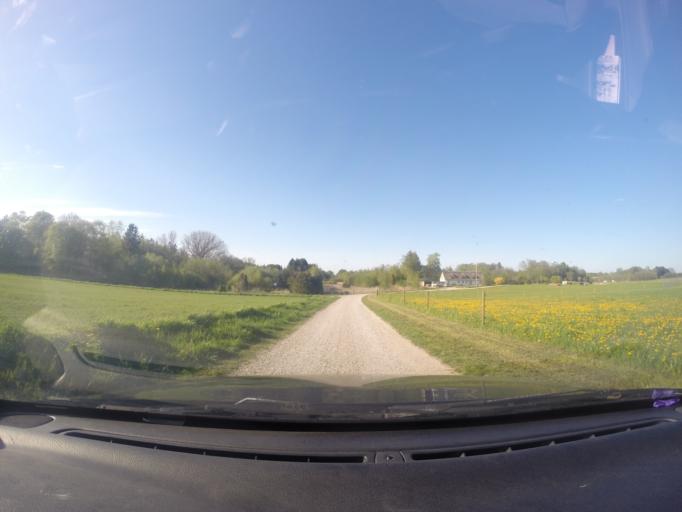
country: DK
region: Capital Region
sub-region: Hoje-Taastrup Kommune
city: Taastrup
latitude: 55.6830
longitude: 12.2574
